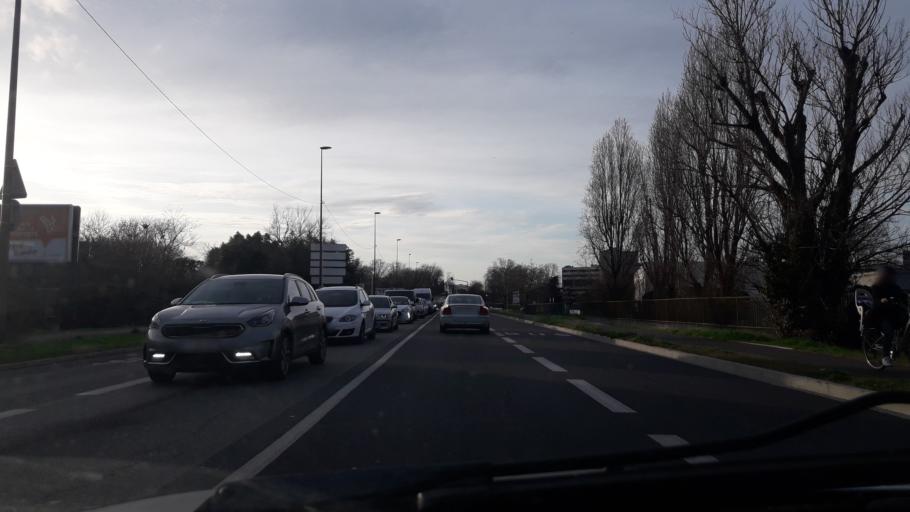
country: FR
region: Midi-Pyrenees
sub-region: Departement de la Haute-Garonne
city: Portet-sur-Garonne
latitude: 43.5584
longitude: 1.4008
